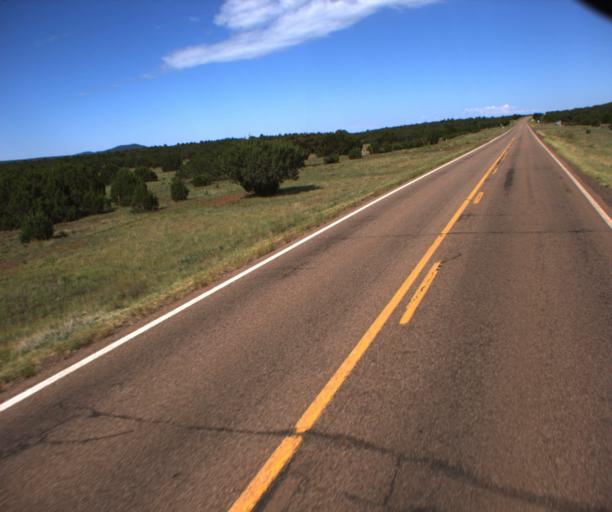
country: US
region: Arizona
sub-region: Navajo County
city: Pinetop-Lakeside
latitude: 34.2756
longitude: -109.7812
